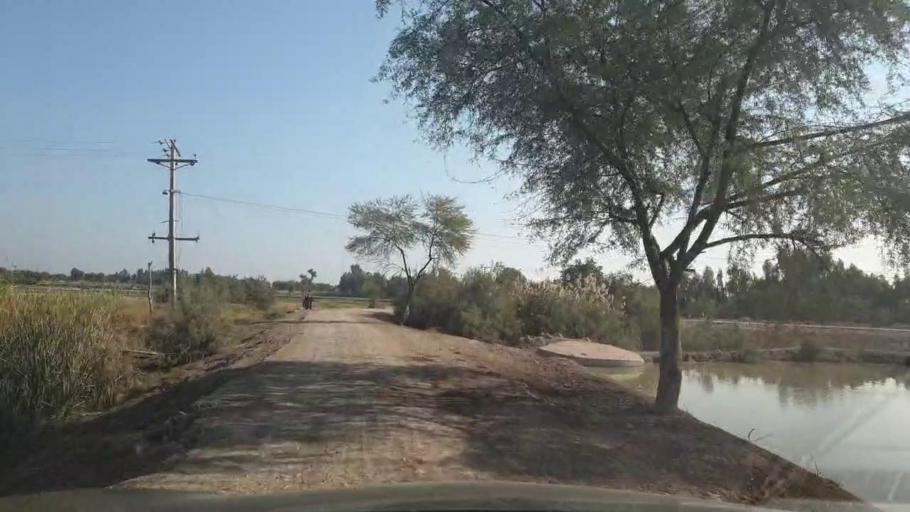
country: PK
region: Sindh
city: Khairpur
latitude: 28.1368
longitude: 69.6012
